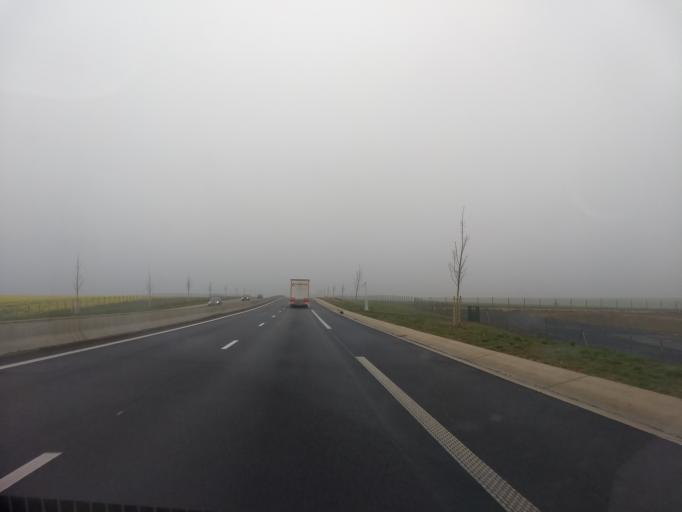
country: FR
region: Nord-Pas-de-Calais
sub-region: Departement du Pas-de-Calais
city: Aubigny-en-Artois
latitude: 50.3396
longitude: 2.6069
